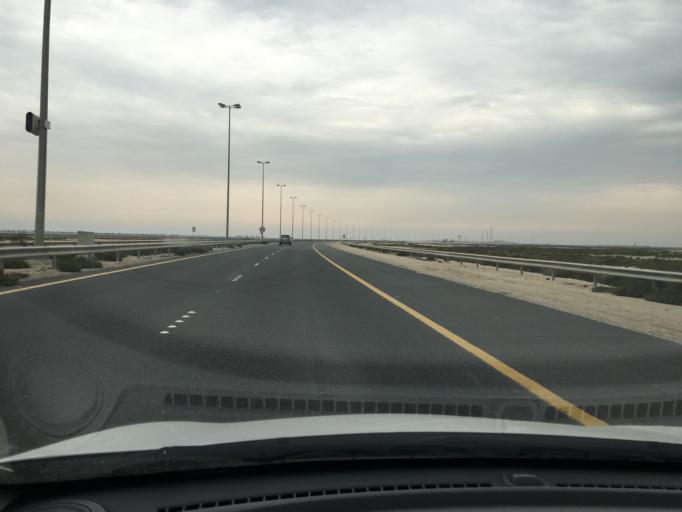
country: BH
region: Central Governorate
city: Dar Kulayb
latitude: 25.8665
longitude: 50.5836
